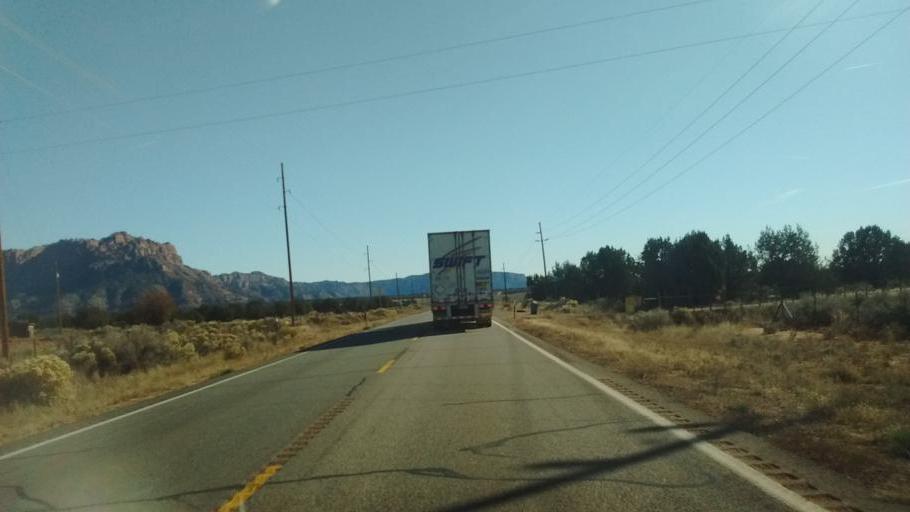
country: US
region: Arizona
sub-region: Mohave County
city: Colorado City
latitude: 37.0364
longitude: -113.0682
